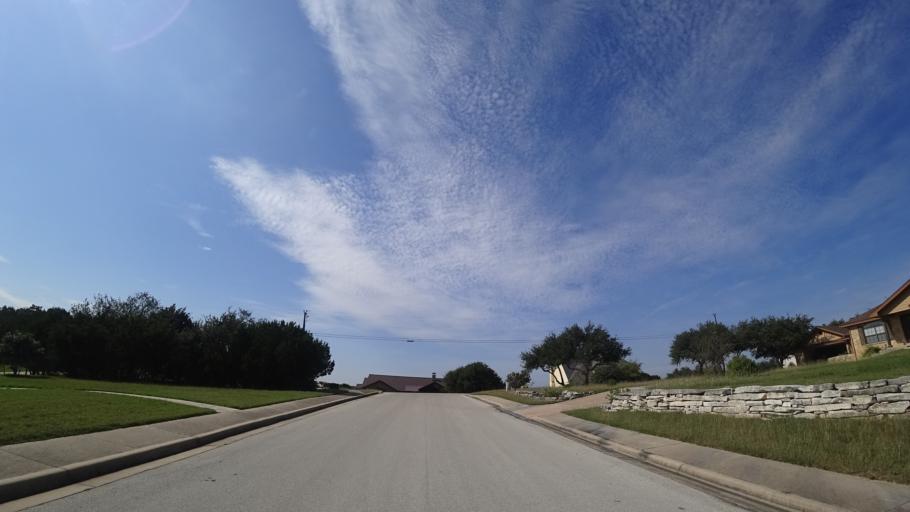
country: US
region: Texas
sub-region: Travis County
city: Bee Cave
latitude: 30.2225
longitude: -97.9357
